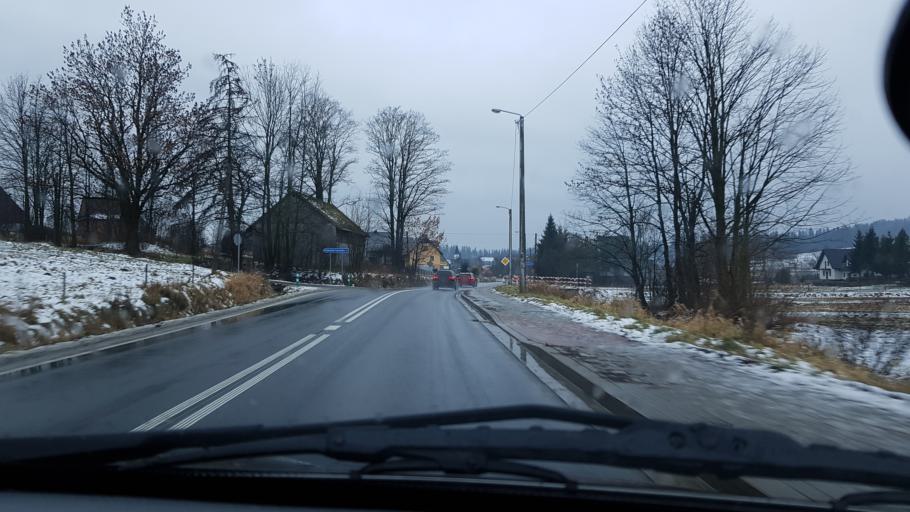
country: PL
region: Lesser Poland Voivodeship
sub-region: Powiat nowotarski
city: Sieniawa
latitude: 49.5023
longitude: 19.8864
